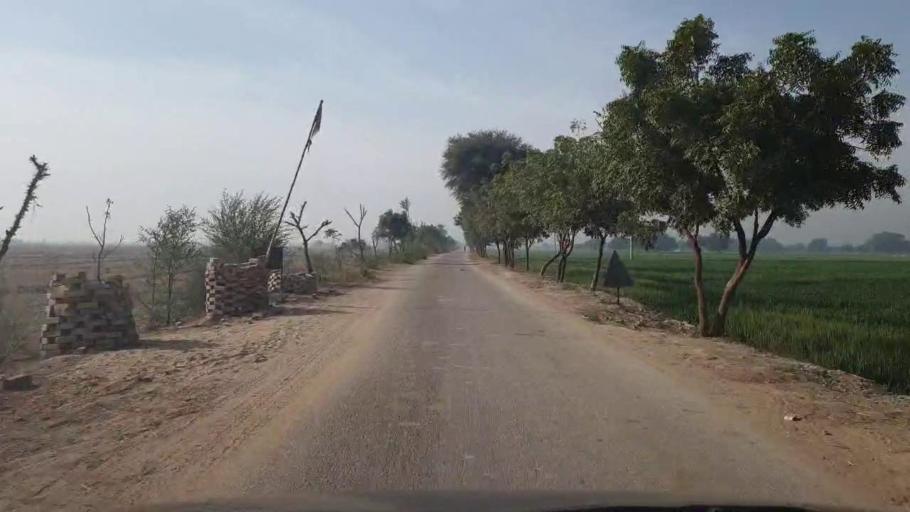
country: PK
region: Sindh
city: Umarkot
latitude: 25.3556
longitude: 69.7000
